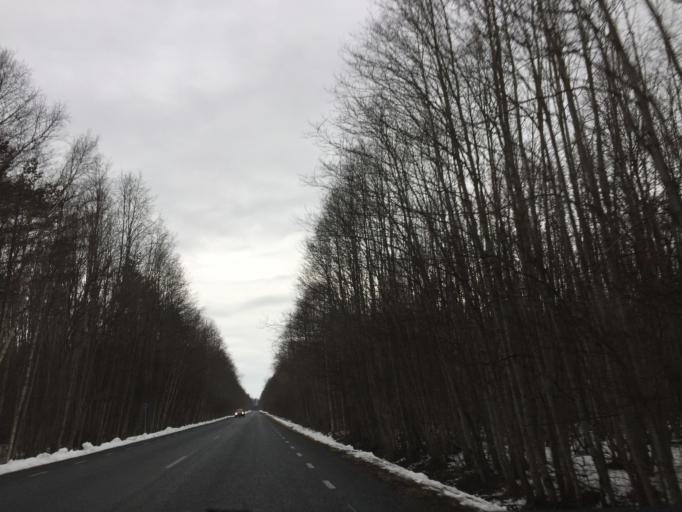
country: EE
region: Saare
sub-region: Orissaare vald
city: Orissaare
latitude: 58.5614
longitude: 22.7723
